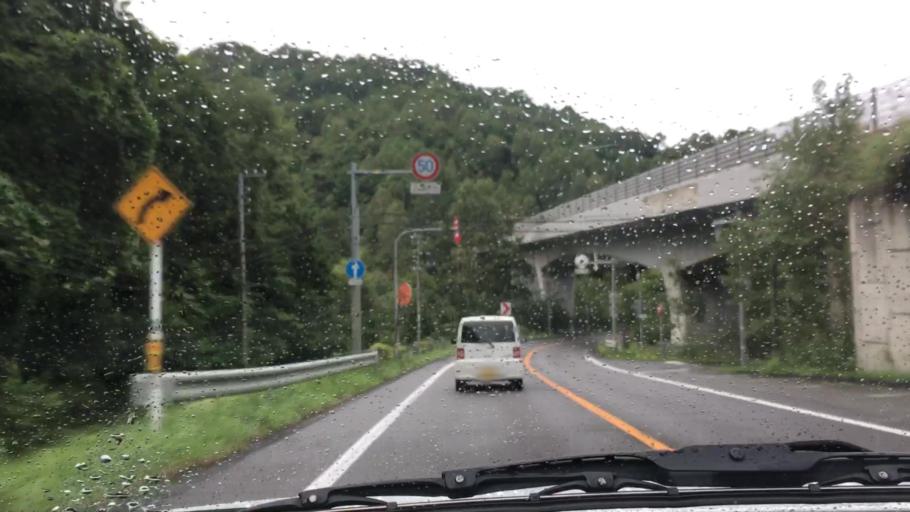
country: JP
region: Hokkaido
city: Date
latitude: 42.5842
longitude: 140.7271
